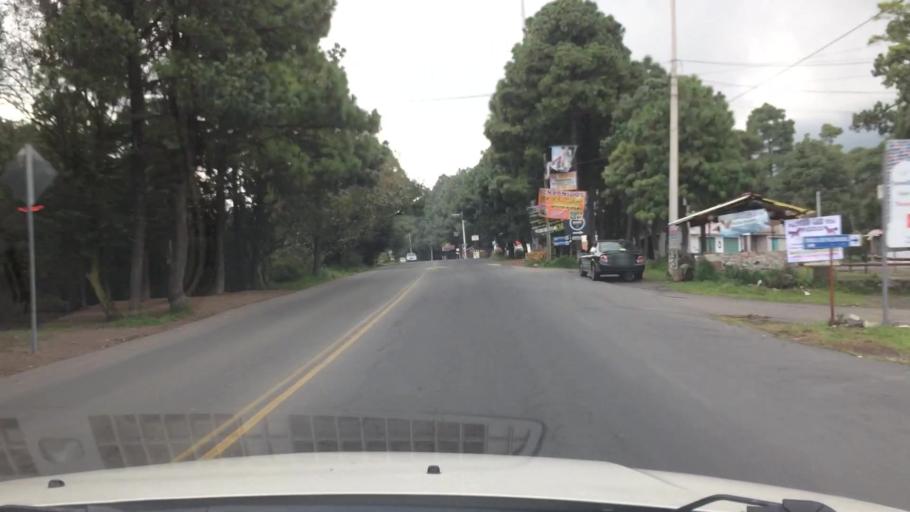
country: MX
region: Mexico City
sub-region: Tlalpan
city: Lomas de Tepemecatl
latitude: 19.2455
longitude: -99.2416
